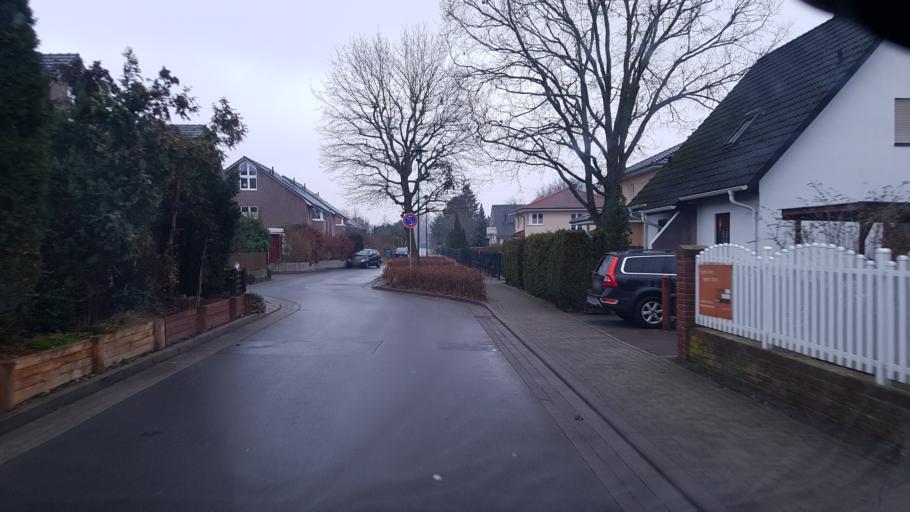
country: DE
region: Brandenburg
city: Stahnsdorf
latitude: 52.3765
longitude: 13.2160
